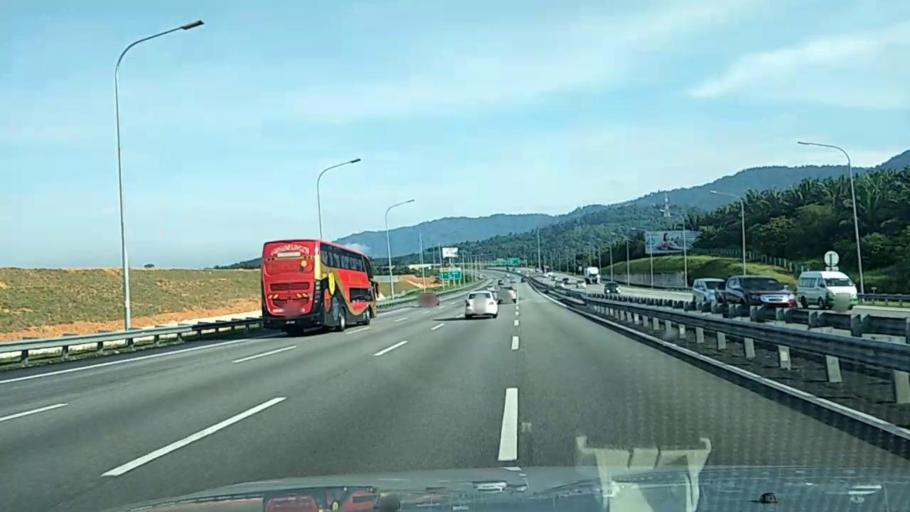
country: MY
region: Negeri Sembilan
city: Seremban
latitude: 2.7350
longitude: 101.8897
